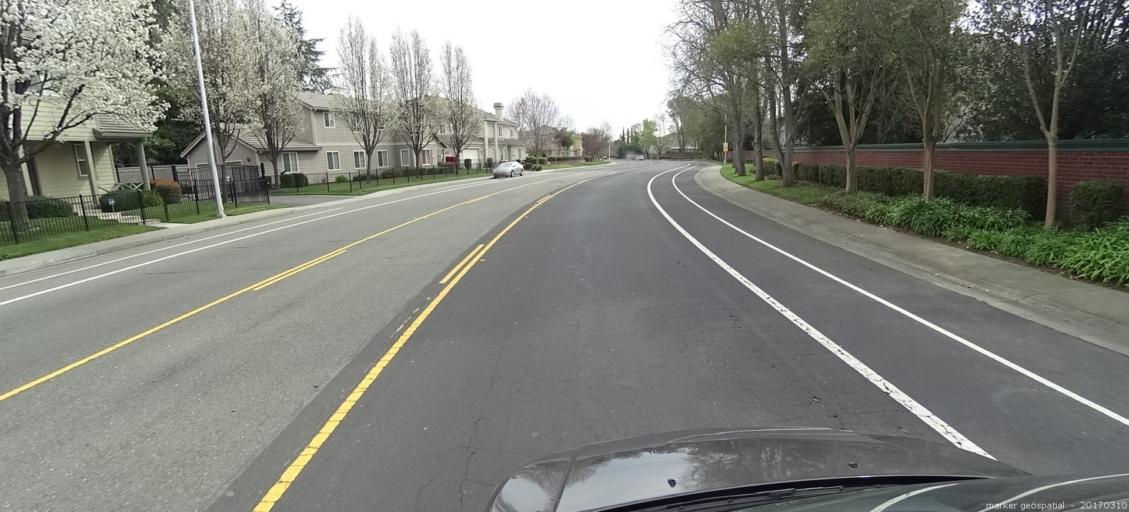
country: US
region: California
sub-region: Sacramento County
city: Parkway
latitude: 38.4841
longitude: -121.5302
